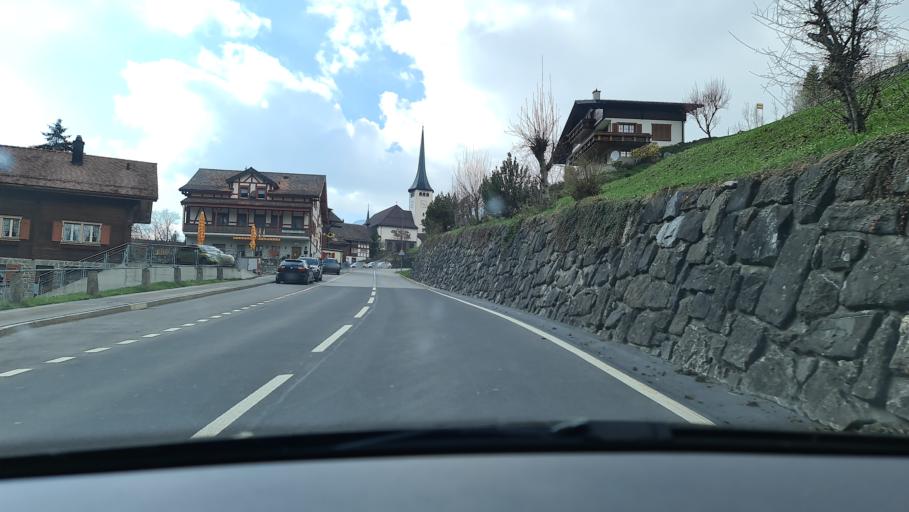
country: CH
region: Uri
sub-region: Uri
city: Burglen
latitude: 46.8718
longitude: 8.7296
